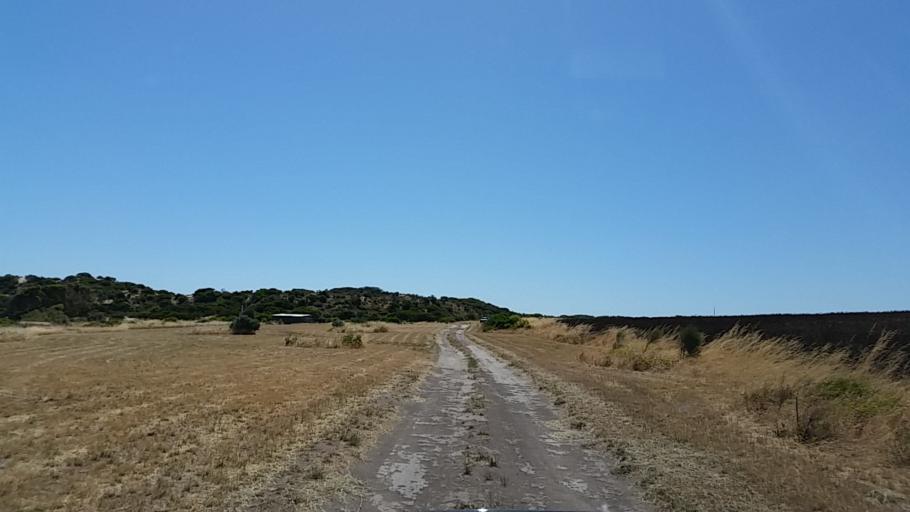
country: AU
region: South Australia
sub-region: Yorke Peninsula
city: Honiton
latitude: -35.2359
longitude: 137.1190
